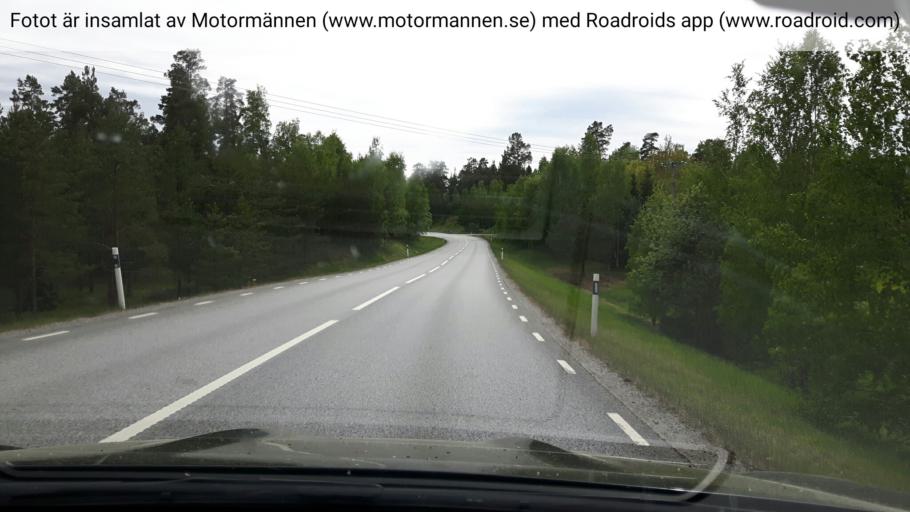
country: SE
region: Stockholm
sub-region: Norrtalje Kommun
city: Norrtalje
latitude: 59.6718
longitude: 18.8406
